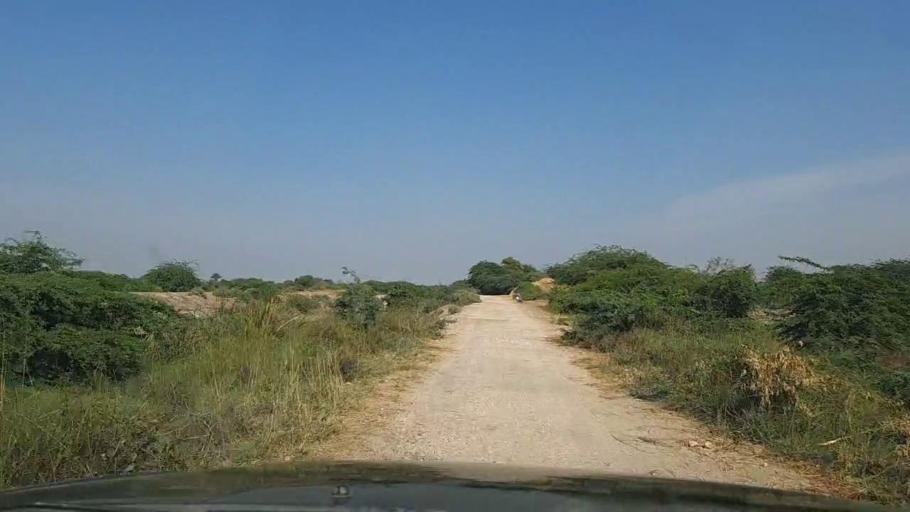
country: PK
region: Sindh
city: Thatta
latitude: 24.7141
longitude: 67.7943
